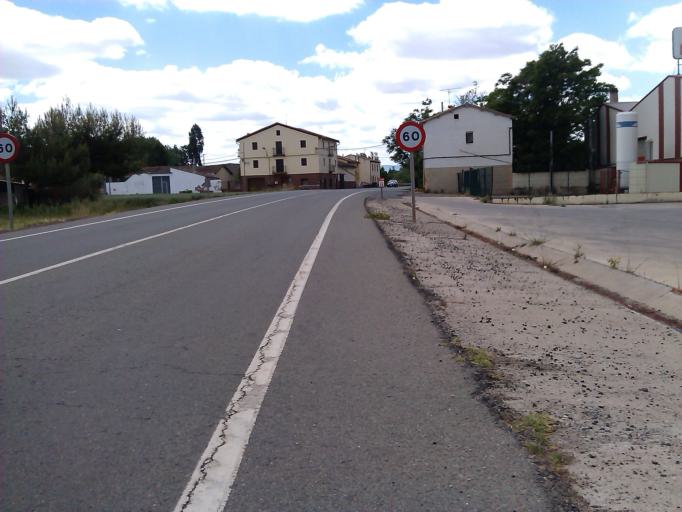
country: ES
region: La Rioja
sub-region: Provincia de La Rioja
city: Aleson
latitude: 42.4093
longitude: -2.6891
